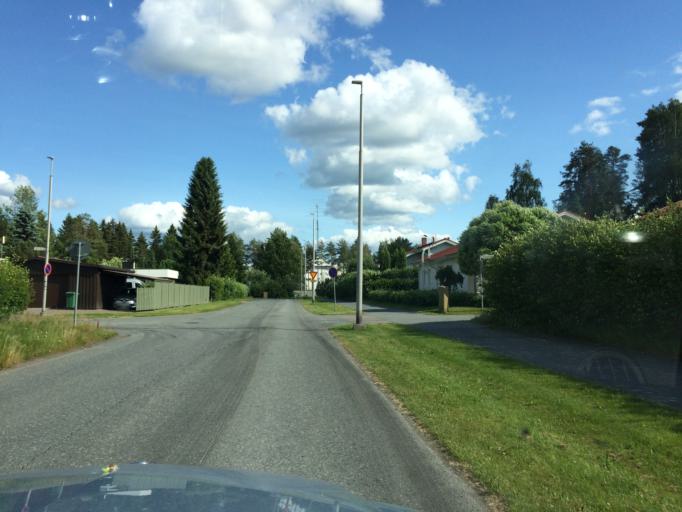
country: FI
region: Haeme
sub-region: Haemeenlinna
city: Haemeenlinna
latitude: 60.9839
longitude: 24.4007
